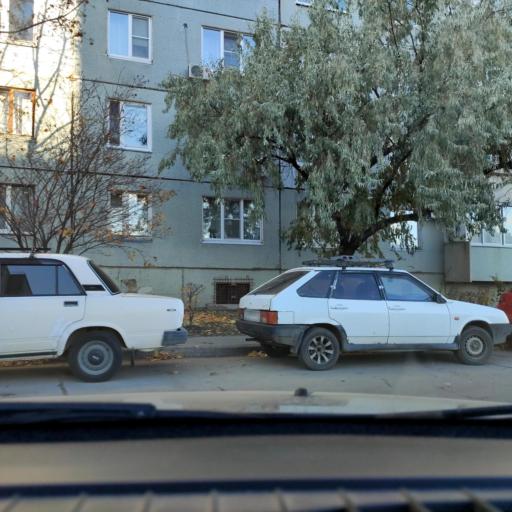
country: RU
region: Samara
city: Tol'yatti
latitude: 53.5420
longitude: 49.3543
